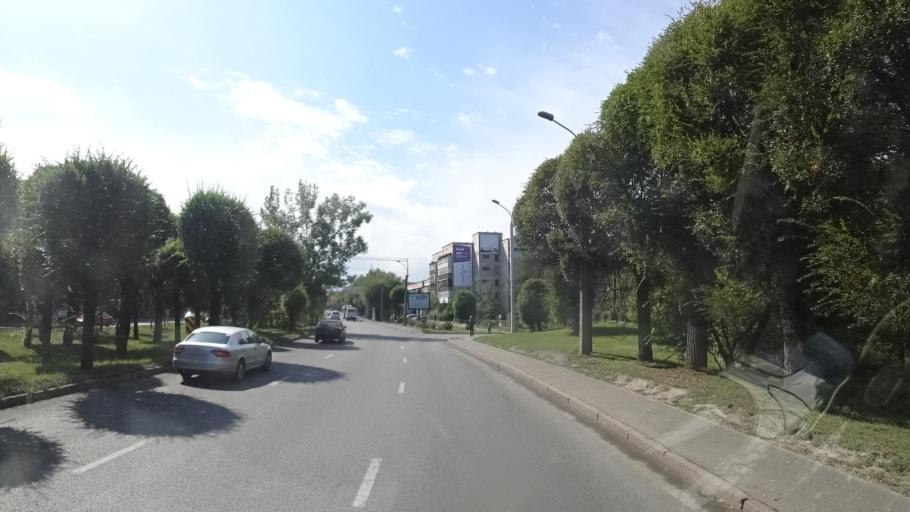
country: KZ
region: Almaty Oblysy
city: Pervomayskiy
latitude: 43.3323
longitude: 76.9783
